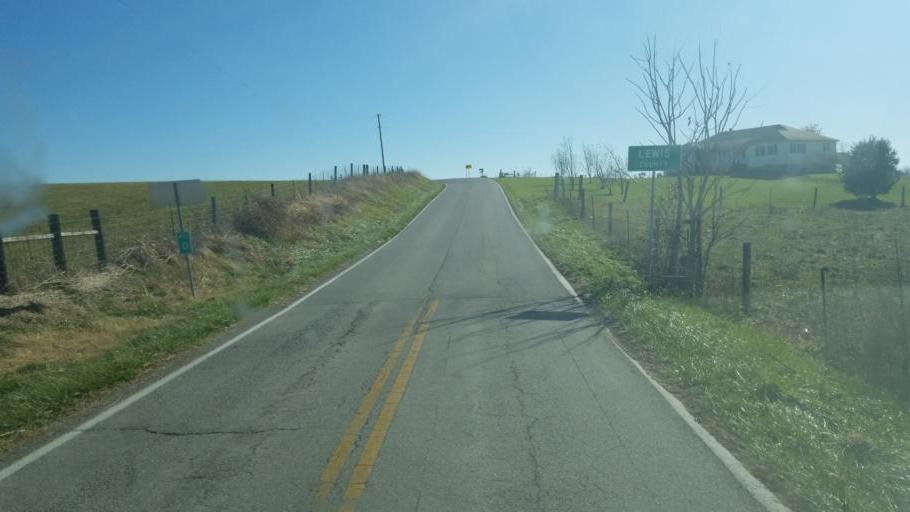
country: US
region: Kentucky
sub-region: Mason County
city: Maysville
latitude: 38.5431
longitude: -83.6383
